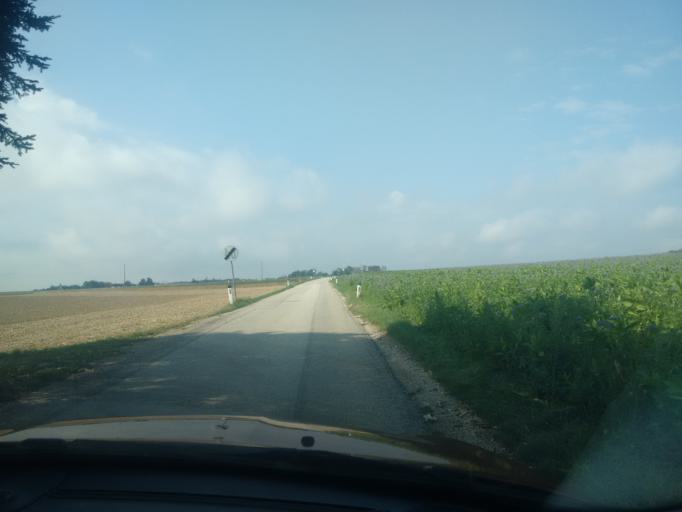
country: AT
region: Upper Austria
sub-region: Wels-Land
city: Steinhaus
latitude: 48.1099
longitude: 14.0089
